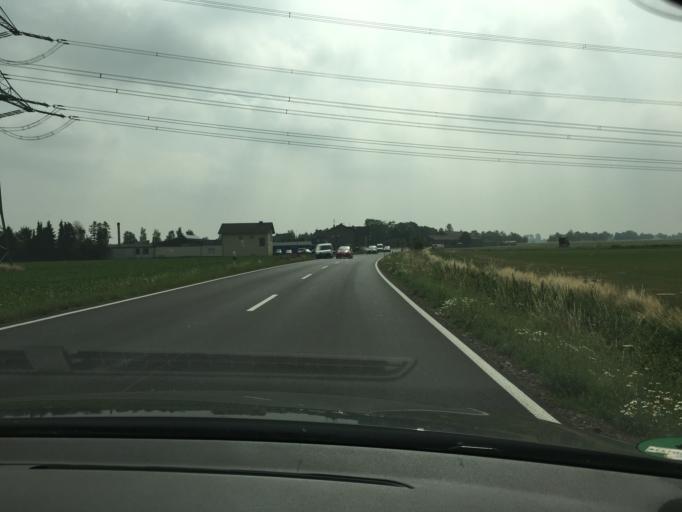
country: DE
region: North Rhine-Westphalia
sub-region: Regierungsbezirk Koln
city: Merzenich
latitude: 50.7957
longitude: 6.5287
